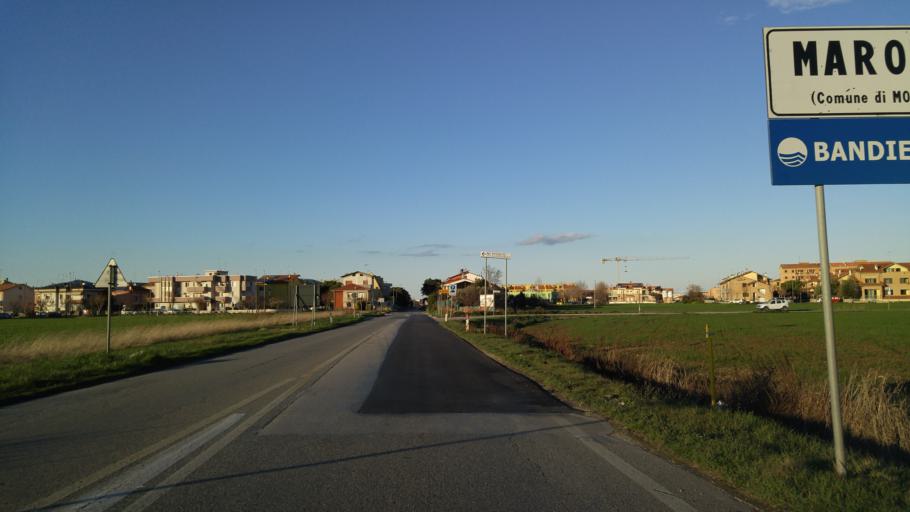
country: IT
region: The Marches
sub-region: Provincia di Pesaro e Urbino
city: Marotta
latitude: 43.7620
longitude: 13.1372
